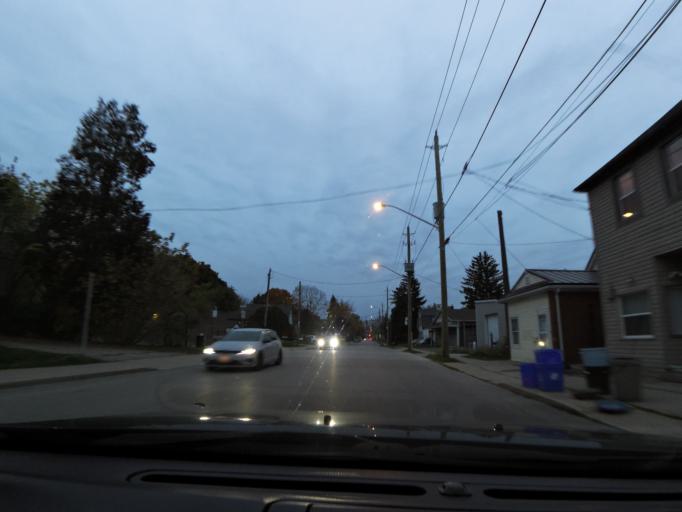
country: CA
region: Ontario
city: Hamilton
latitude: 43.2544
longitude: -79.9210
